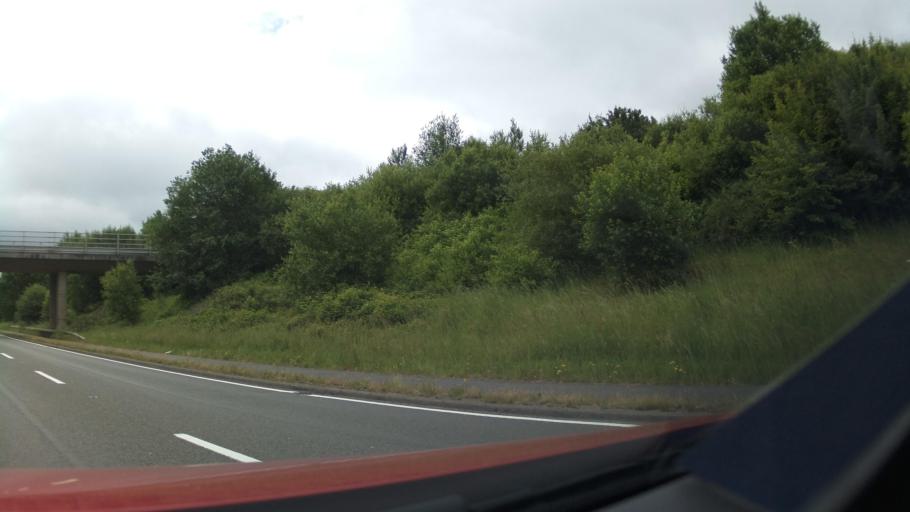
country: GB
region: England
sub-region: Leicestershire
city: Ashby de la Zouch
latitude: 52.7642
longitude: -1.4928
